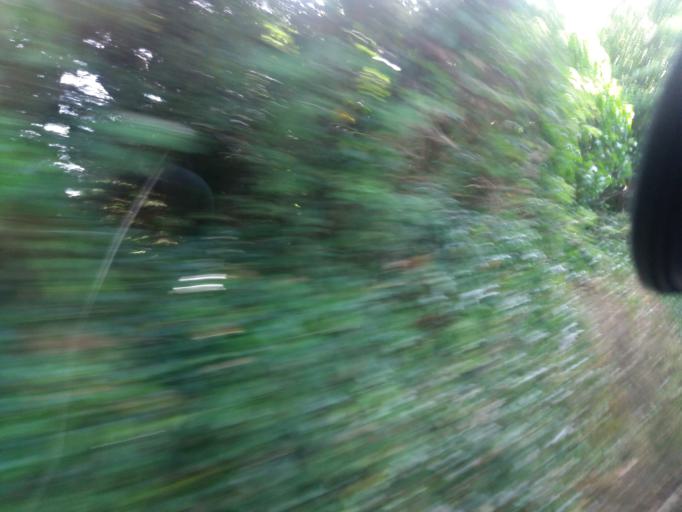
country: IE
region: Leinster
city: Lusk
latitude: 53.5186
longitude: -6.1898
